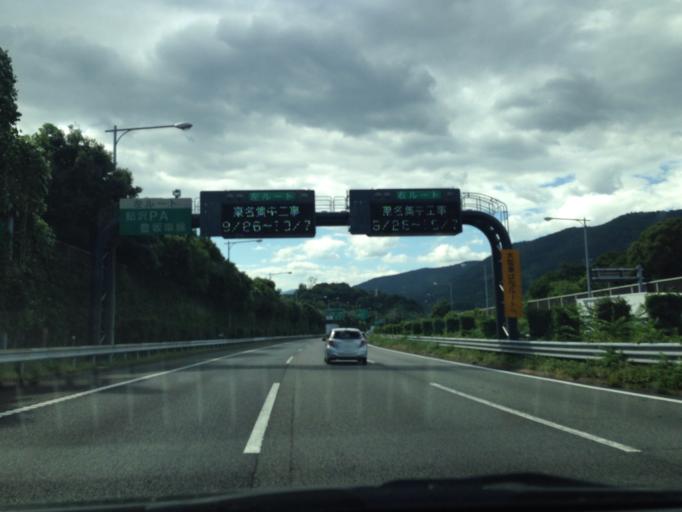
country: JP
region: Kanagawa
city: Hadano
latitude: 35.3407
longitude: 139.1611
